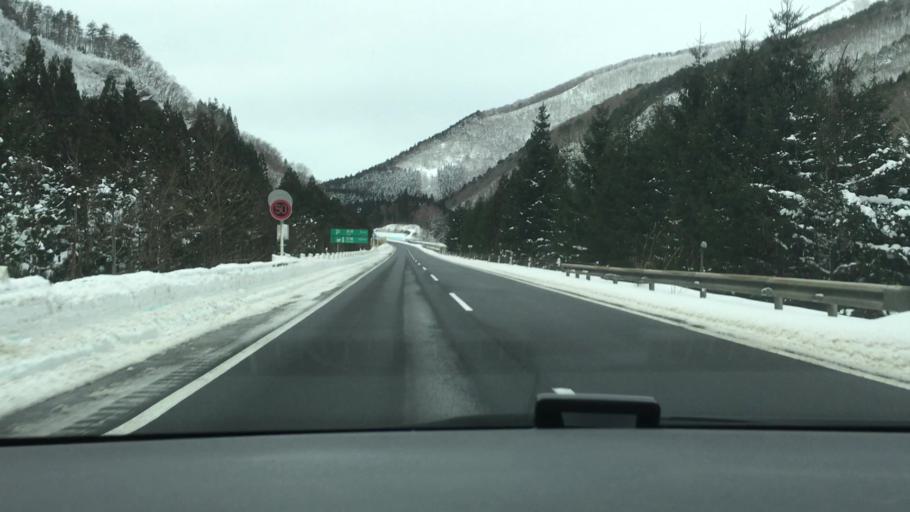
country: JP
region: Akita
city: Hanawa
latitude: 40.1179
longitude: 140.8569
